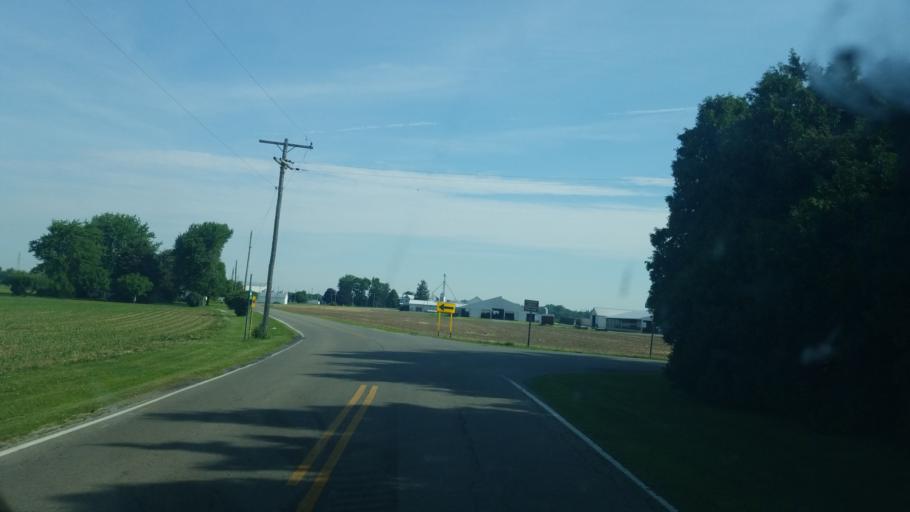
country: US
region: Ohio
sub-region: Hancock County
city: Findlay
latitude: 41.0216
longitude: -83.5880
